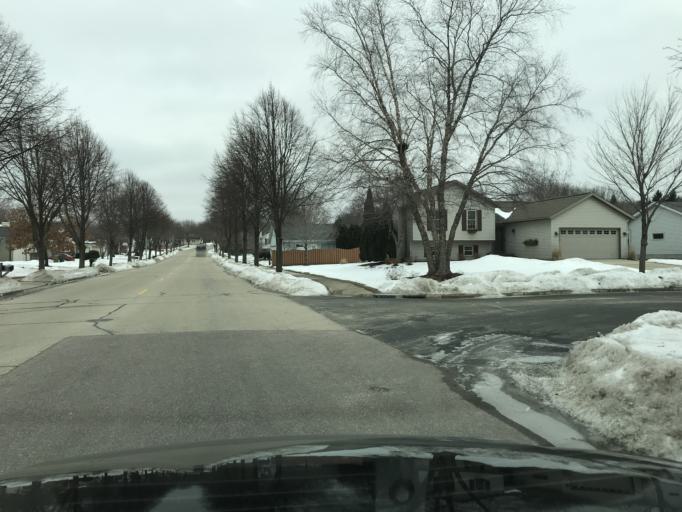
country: US
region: Wisconsin
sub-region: Dane County
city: Monona
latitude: 43.0742
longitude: -89.2829
